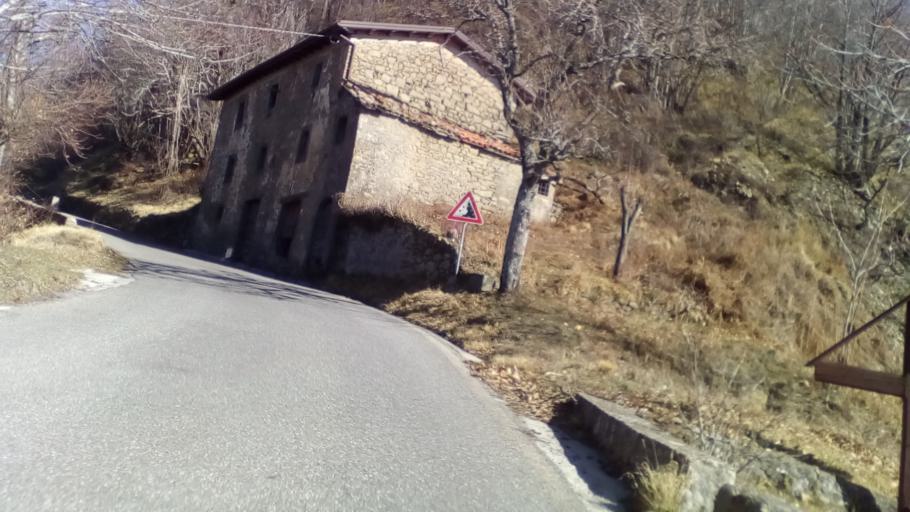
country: IT
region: Tuscany
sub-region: Provincia di Lucca
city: Castiglione di Garfagnana
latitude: 44.1627
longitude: 10.4416
